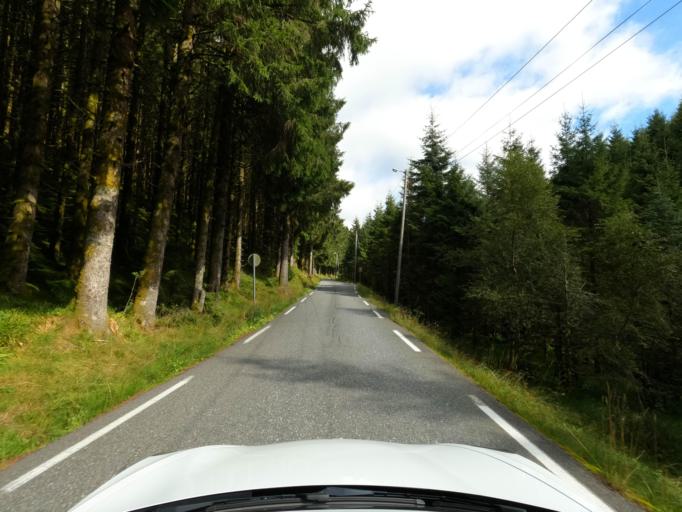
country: NO
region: Hordaland
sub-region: Os
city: Syfteland
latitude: 60.3027
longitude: 5.4499
